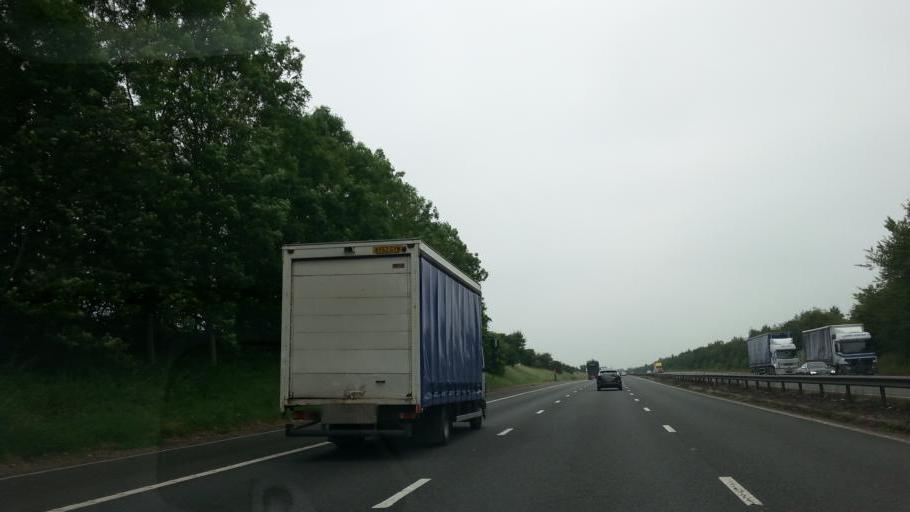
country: GB
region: England
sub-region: Leicestershire
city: Hinckley
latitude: 52.4872
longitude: -1.3912
